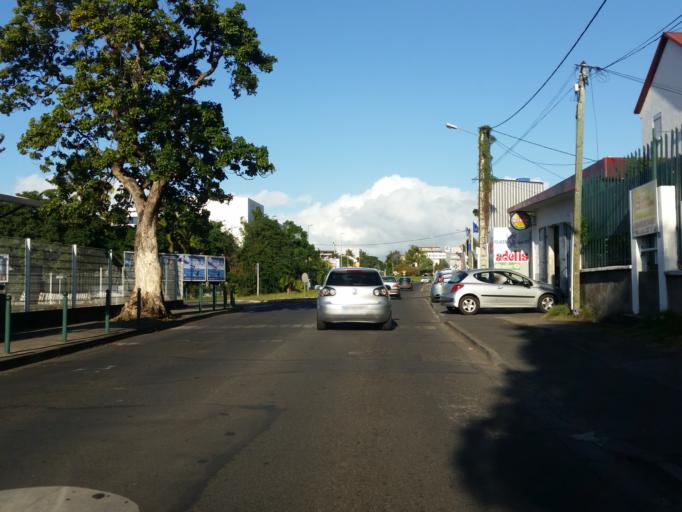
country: RE
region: Reunion
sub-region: Reunion
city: Saint-Denis
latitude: -20.8986
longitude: 55.4958
